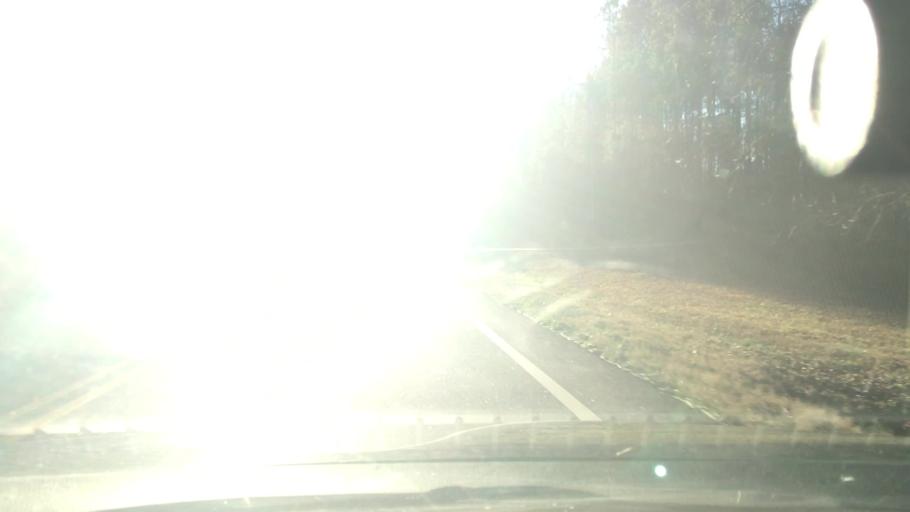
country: US
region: Georgia
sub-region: Coweta County
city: Senoia
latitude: 33.2636
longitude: -84.5187
